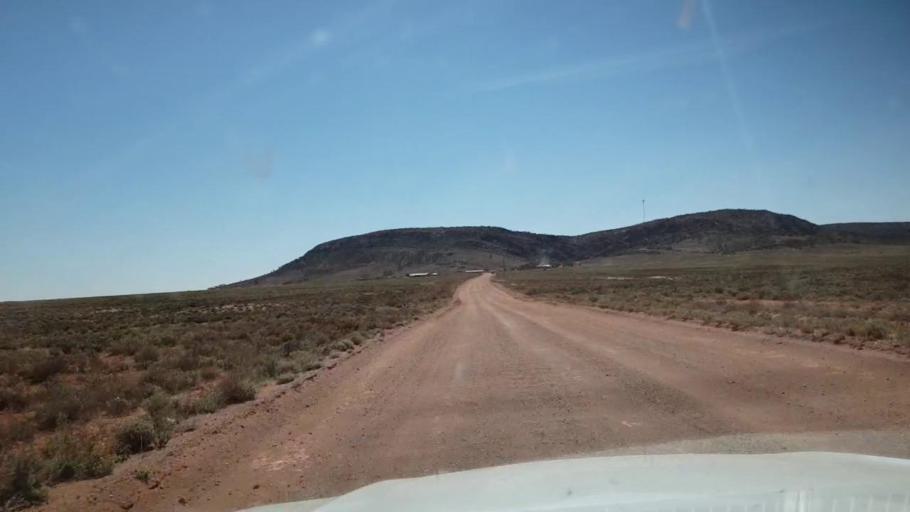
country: AU
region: South Australia
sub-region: Whyalla
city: Whyalla
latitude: -32.6935
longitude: 137.1301
